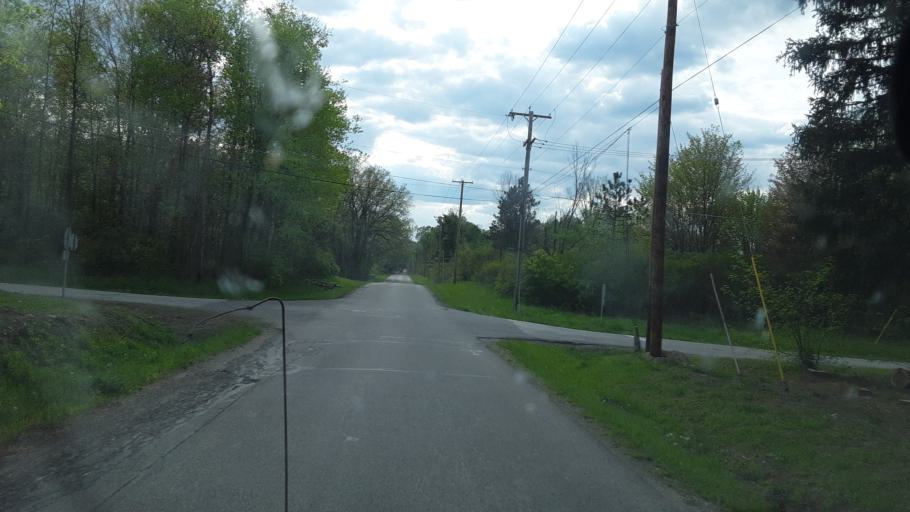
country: US
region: Ohio
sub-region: Portage County
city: Garrettsville
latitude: 41.3478
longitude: -81.0216
